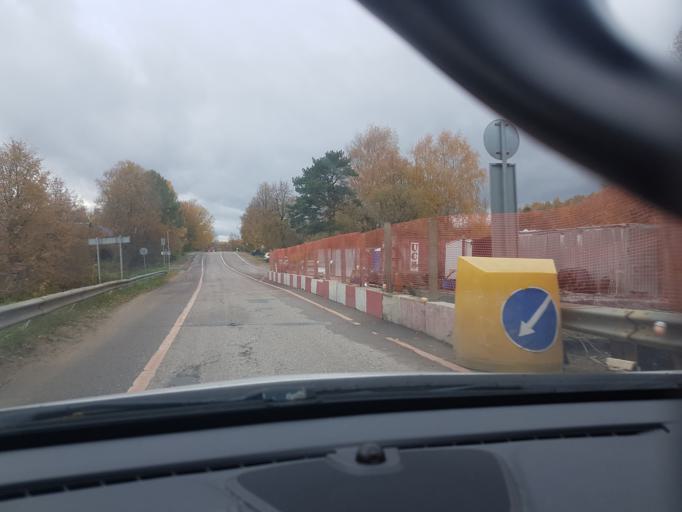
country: RU
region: Moskovskaya
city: Novopetrovskoye
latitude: 56.0081
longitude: 36.3493
